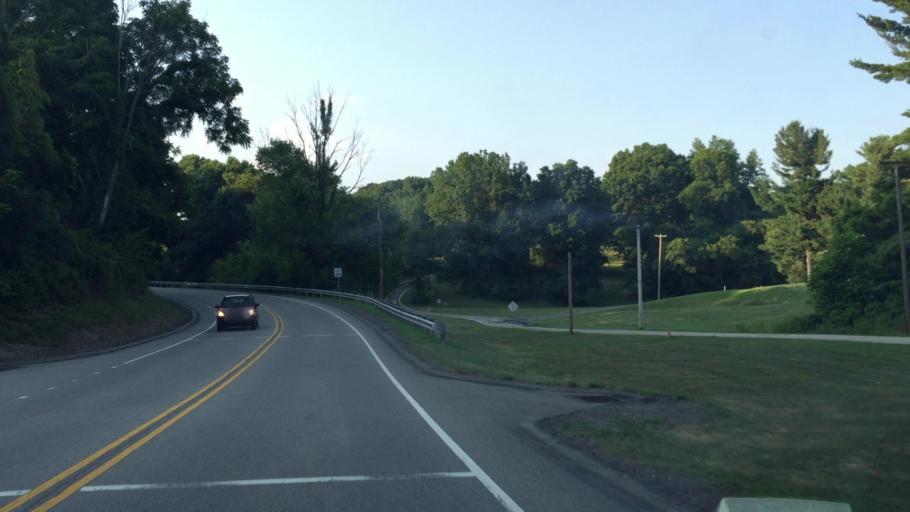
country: US
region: Pennsylvania
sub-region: Allegheny County
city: South Park Township
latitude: 40.3083
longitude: -79.9961
